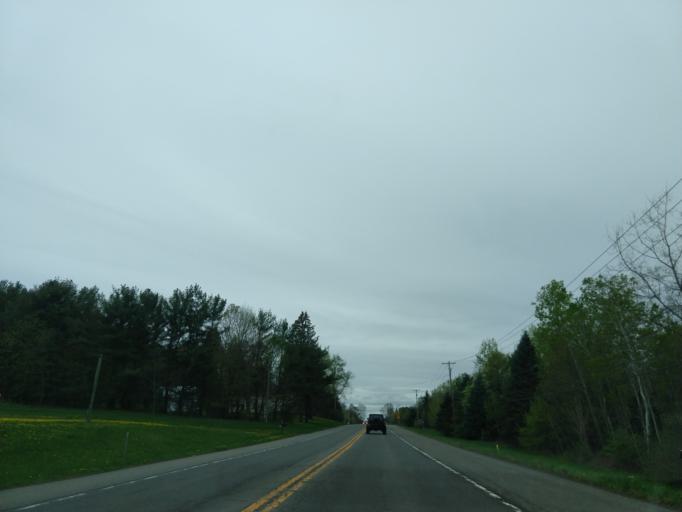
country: US
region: New York
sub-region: Tompkins County
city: Northeast Ithaca
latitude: 42.4741
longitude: -76.3938
